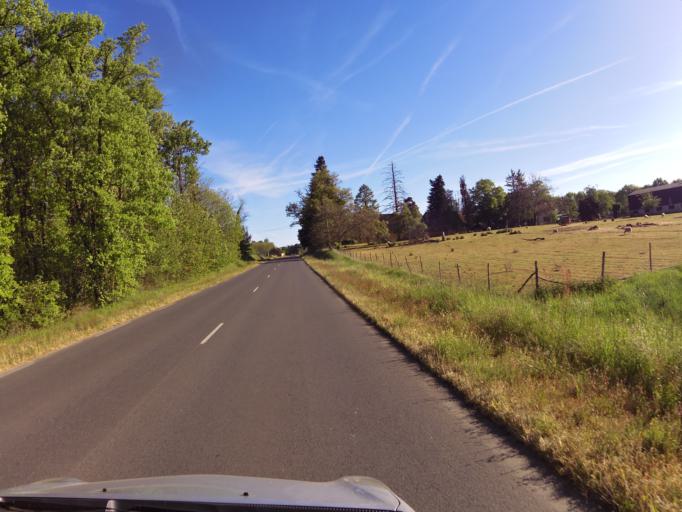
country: FR
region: Aquitaine
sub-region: Departement de la Dordogne
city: Sarlat-la-Caneda
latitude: 44.9854
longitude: 1.2396
